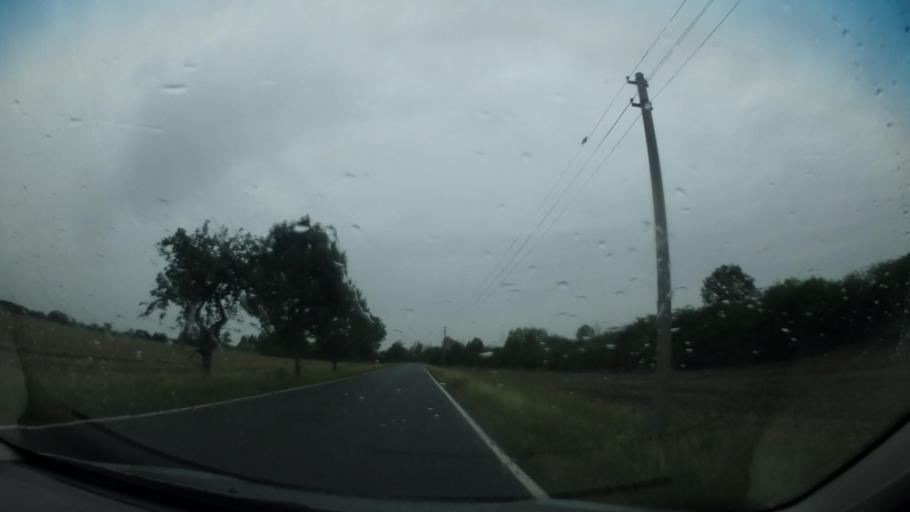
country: CZ
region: Central Bohemia
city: Loucen
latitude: 50.2350
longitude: 14.9738
